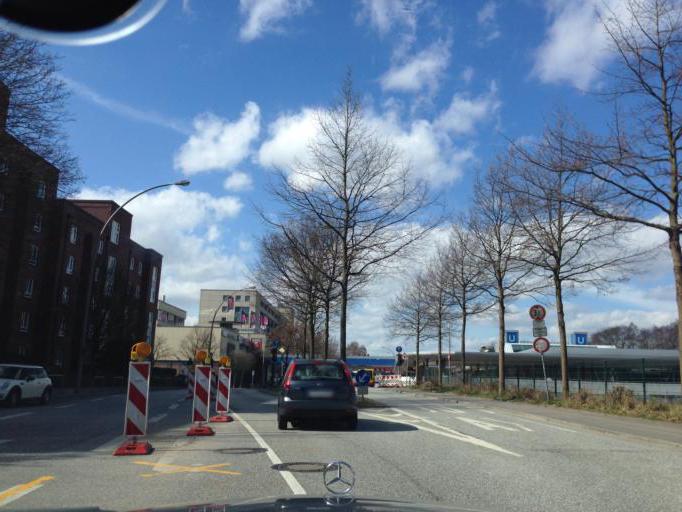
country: DE
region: Hamburg
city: Wandsbek
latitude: 53.5417
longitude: 10.1086
